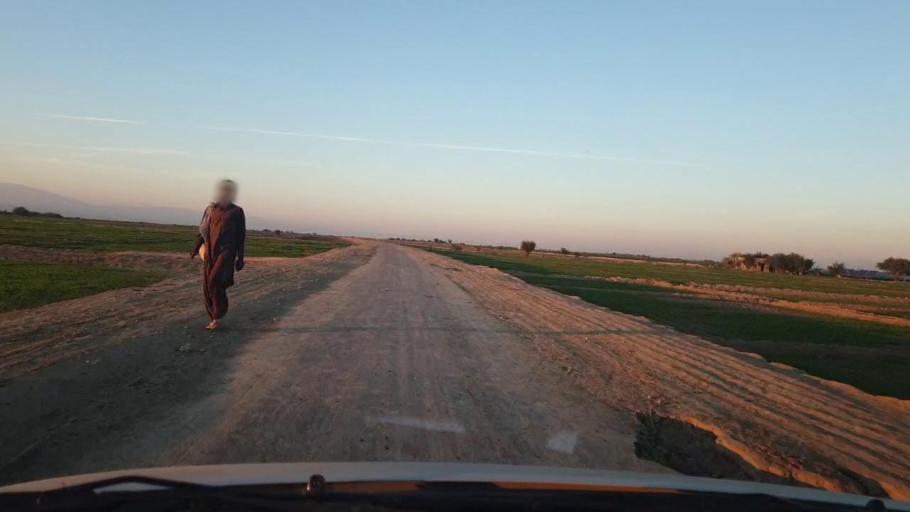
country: PK
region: Sindh
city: Johi
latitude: 26.8344
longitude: 67.4421
